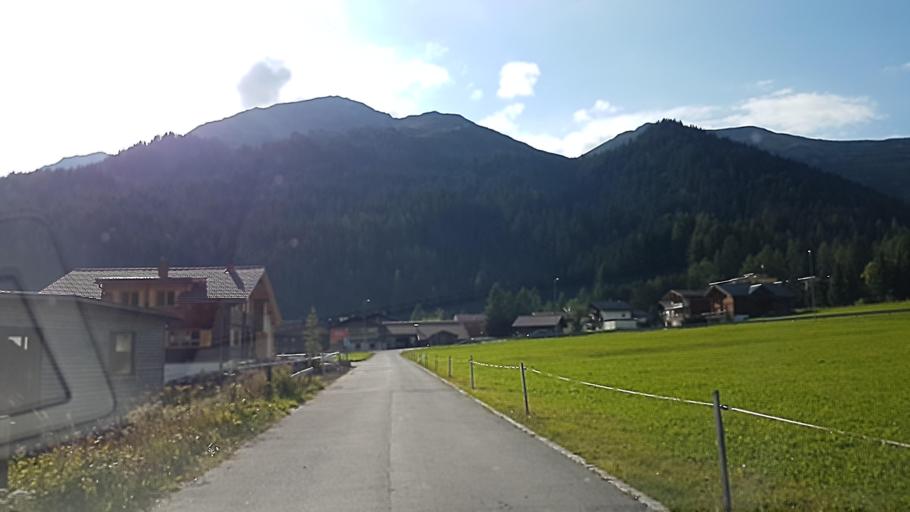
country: CH
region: Grisons
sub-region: Praettigau/Davos District
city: Davos
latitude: 46.8268
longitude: 9.8573
